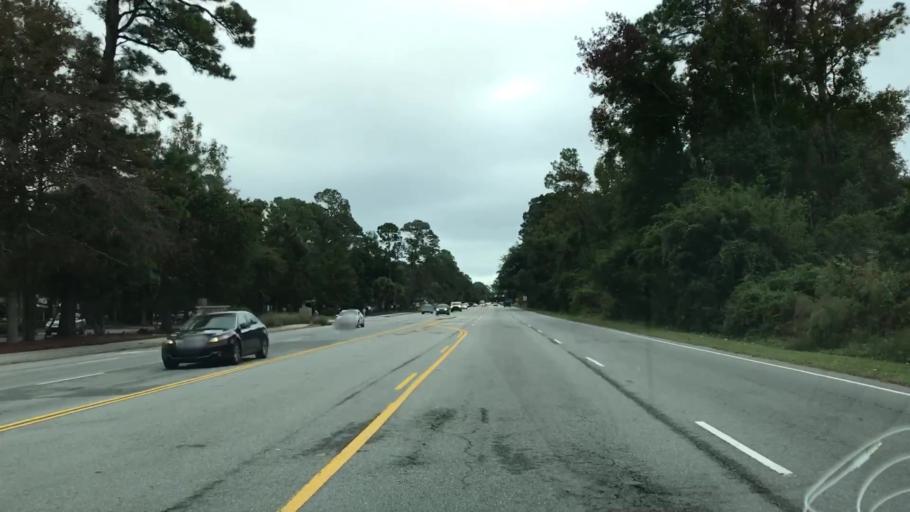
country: US
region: South Carolina
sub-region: Beaufort County
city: Hilton Head Island
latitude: 32.1618
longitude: -80.7680
